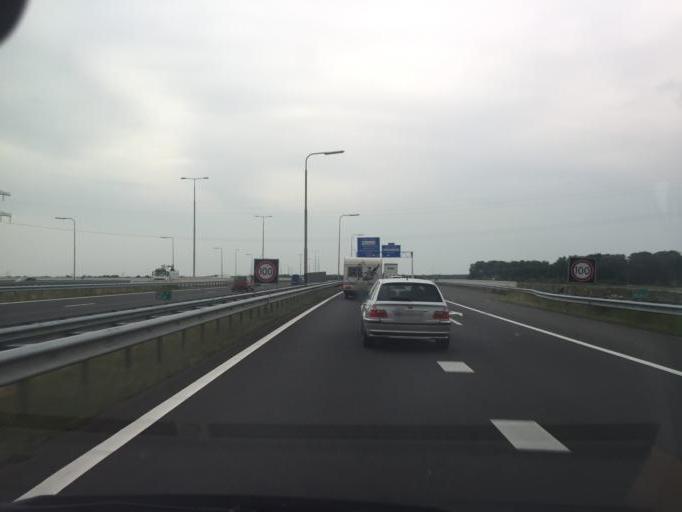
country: NL
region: Limburg
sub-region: Gemeente Venlo
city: Tegelen
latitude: 51.3872
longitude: 6.1255
